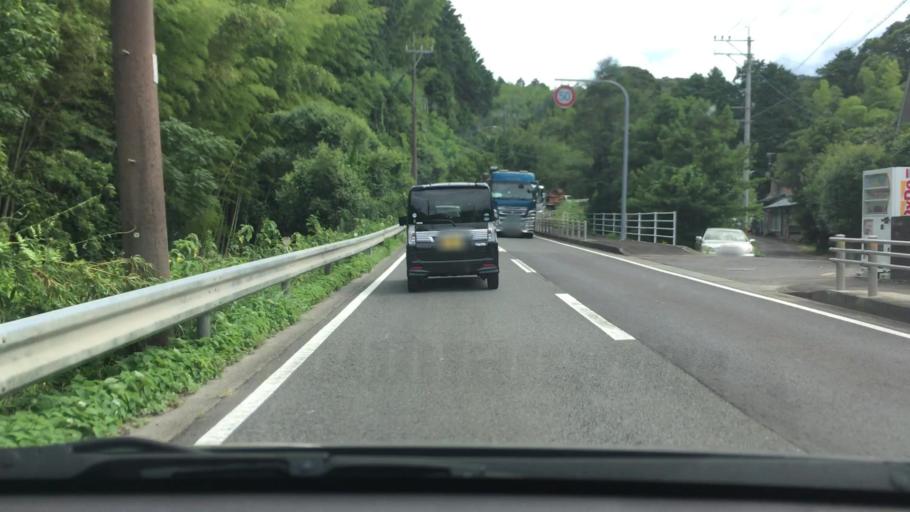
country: JP
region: Nagasaki
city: Togitsu
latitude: 32.9323
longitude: 129.7834
